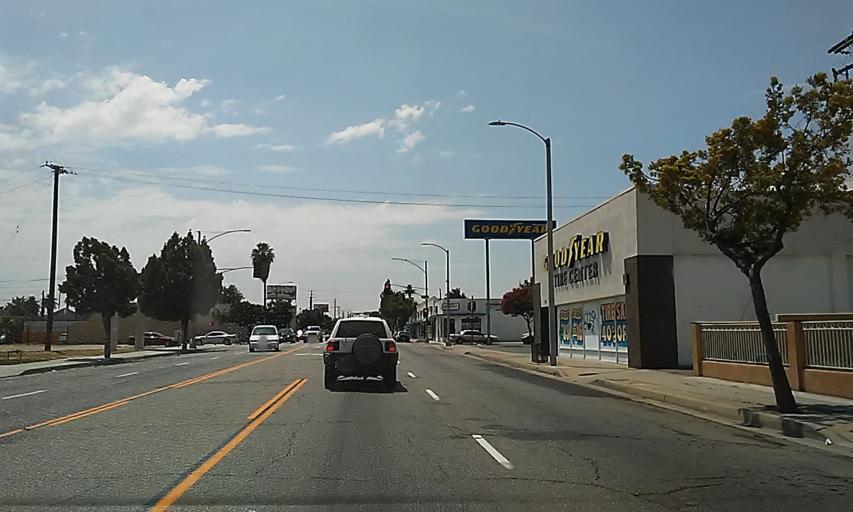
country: US
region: California
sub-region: San Bernardino County
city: San Bernardino
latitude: 34.1214
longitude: -117.2956
